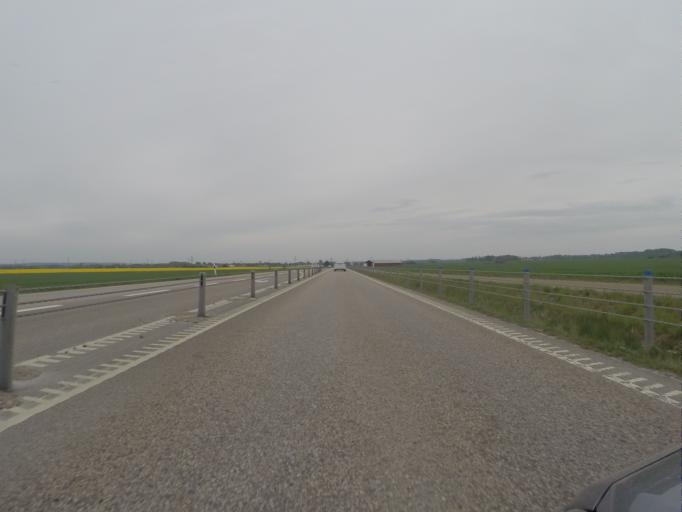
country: SE
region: Skane
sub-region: Helsingborg
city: Morarp
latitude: 56.0896
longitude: 12.8720
